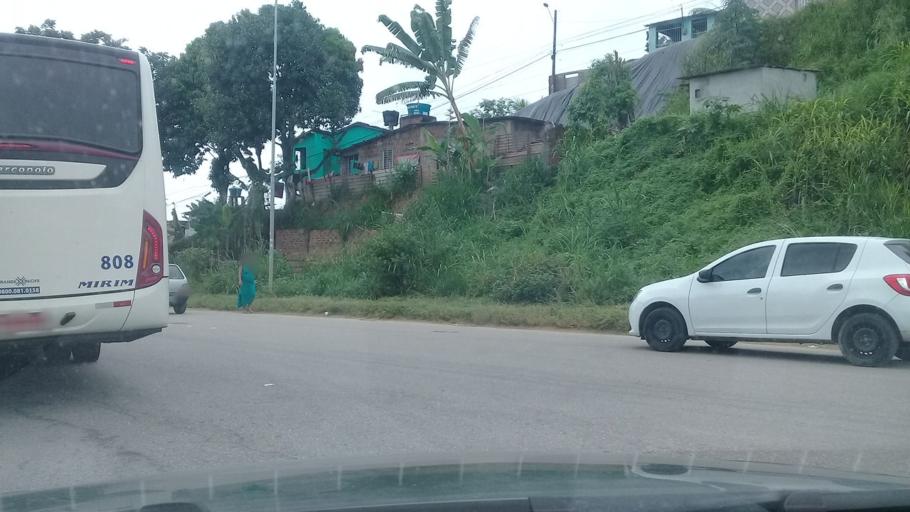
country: BR
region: Pernambuco
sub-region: Jaboatao Dos Guararapes
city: Jaboatao dos Guararapes
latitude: -8.0821
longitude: -34.9917
